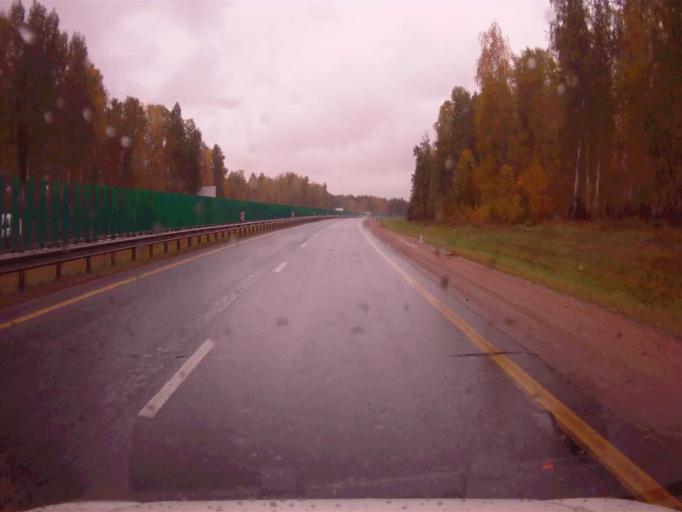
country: RU
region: Chelyabinsk
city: Dolgoderevenskoye
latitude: 55.3354
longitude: 61.3113
